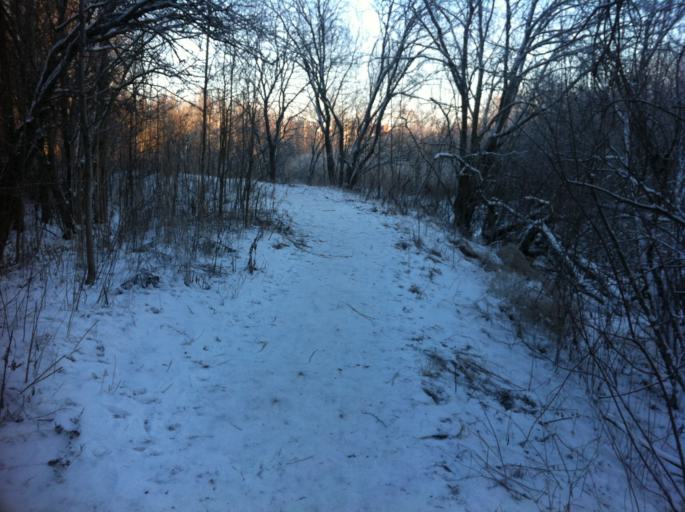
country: RU
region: St.-Petersburg
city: Uritsk
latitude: 59.8545
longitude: 30.1622
